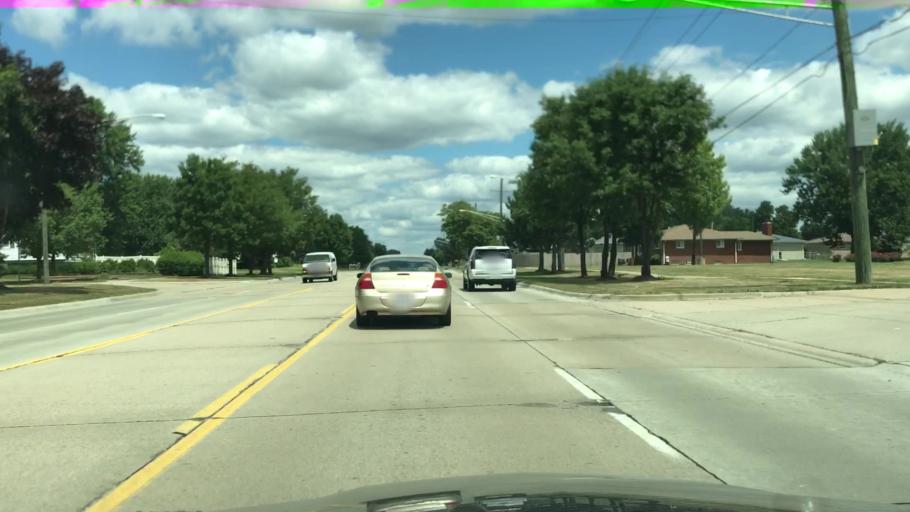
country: US
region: Michigan
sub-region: Macomb County
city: Sterling Heights
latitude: 42.5379
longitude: -83.0686
